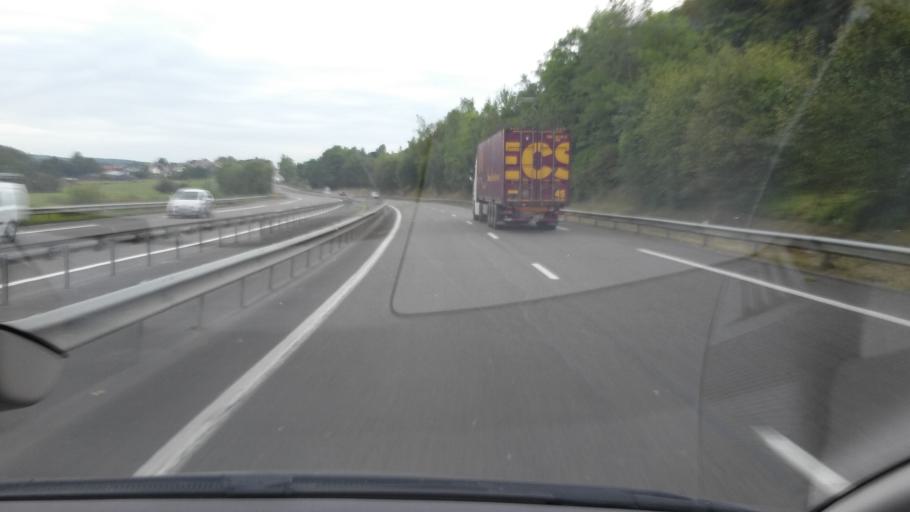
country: FR
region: Champagne-Ardenne
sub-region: Departement des Ardennes
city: La Francheville
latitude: 49.6710
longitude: 4.6504
